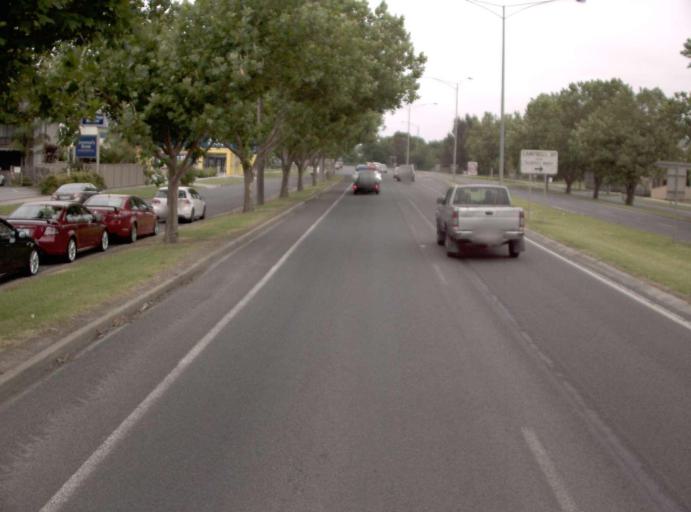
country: AU
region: Victoria
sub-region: Latrobe
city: Traralgon
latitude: -38.1933
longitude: 146.5465
